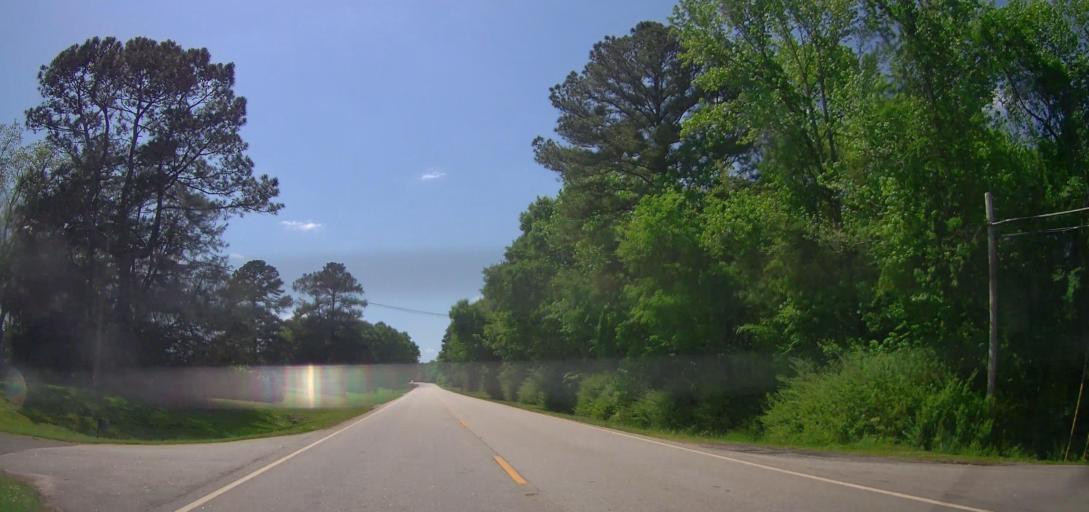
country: US
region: Georgia
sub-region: Putnam County
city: Eatonton
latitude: 33.3402
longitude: -83.3508
